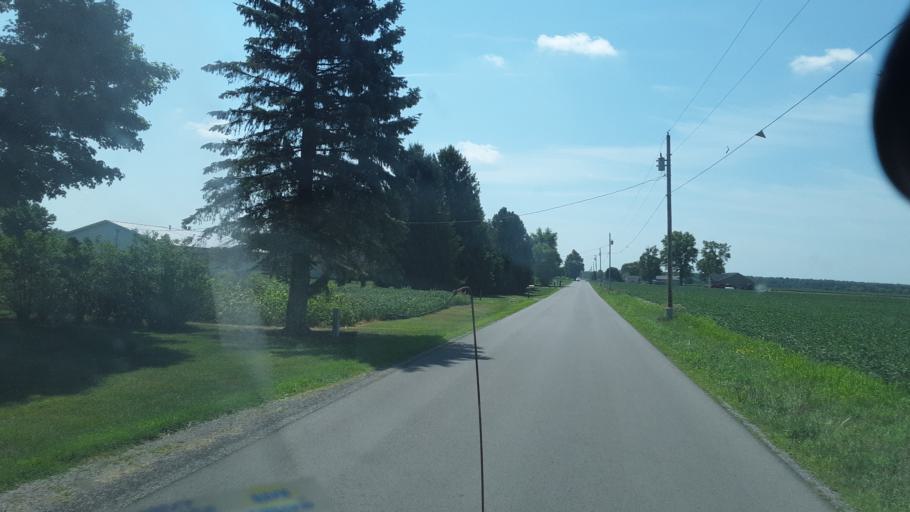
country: US
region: Ohio
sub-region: Hancock County
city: Findlay
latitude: 41.0008
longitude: -83.5161
